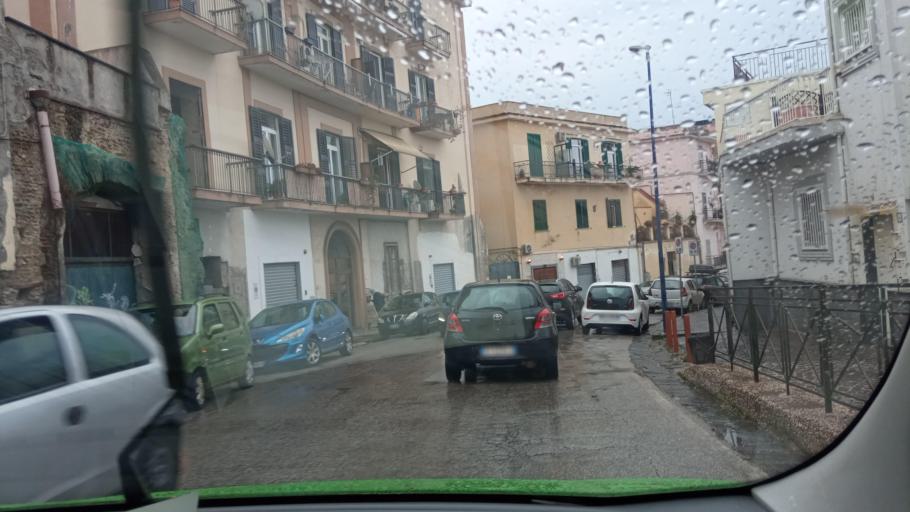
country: IT
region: Campania
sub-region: Provincia di Napoli
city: Pozzuoli
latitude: 40.8276
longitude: 14.1213
